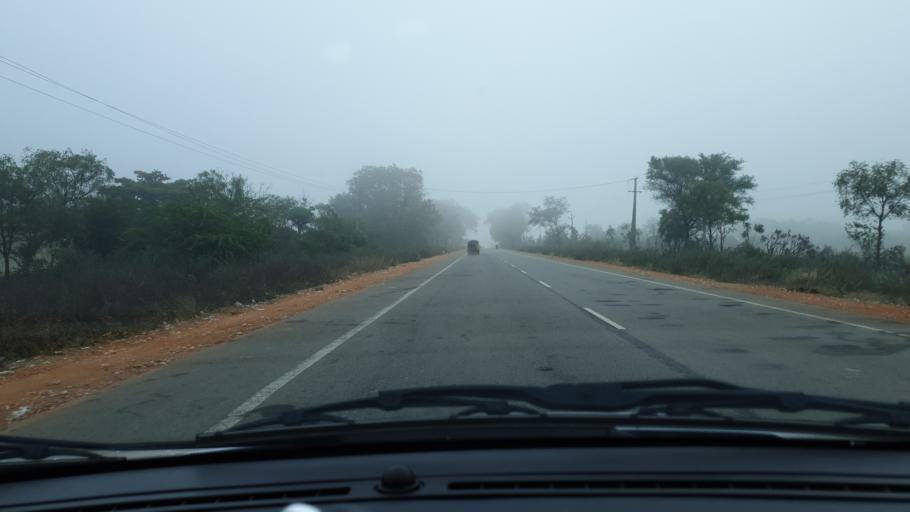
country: IN
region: Telangana
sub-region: Mahbubnagar
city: Nagar Karnul
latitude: 16.6342
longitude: 78.6036
